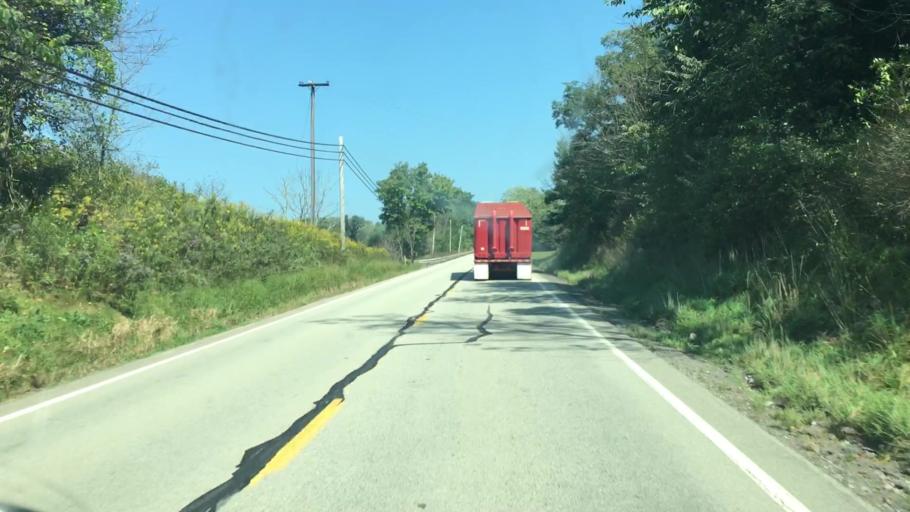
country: US
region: Pennsylvania
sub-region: Washington County
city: Washington
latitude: 40.0740
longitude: -80.2939
